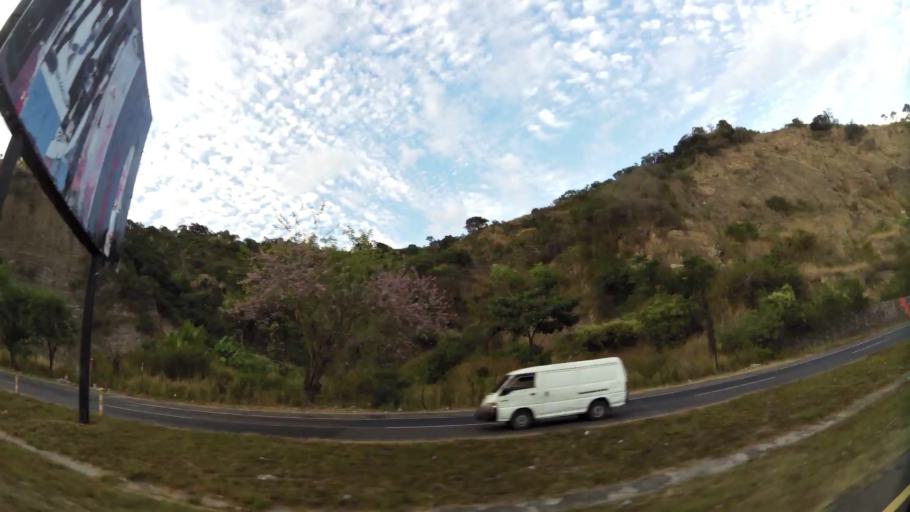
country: SV
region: San Vicente
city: Apastepeque
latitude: 13.6672
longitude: -88.8138
